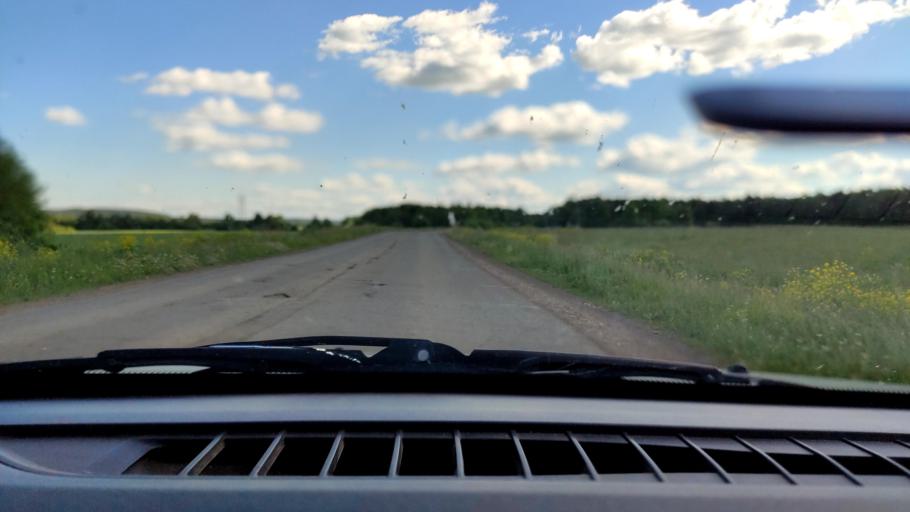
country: RU
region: Perm
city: Uinskoye
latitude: 57.1584
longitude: 56.5709
